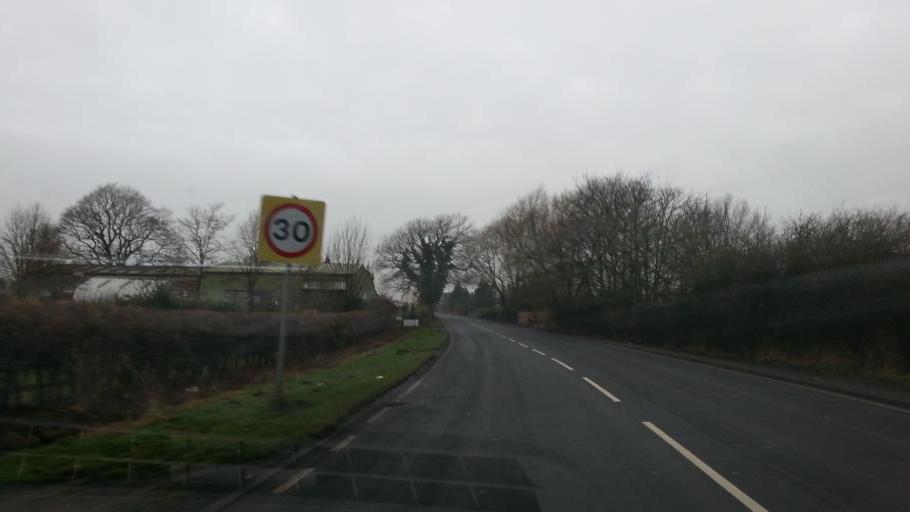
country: GB
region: England
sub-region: City and Borough of Wakefield
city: Badsworth
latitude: 53.6457
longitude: -1.2855
